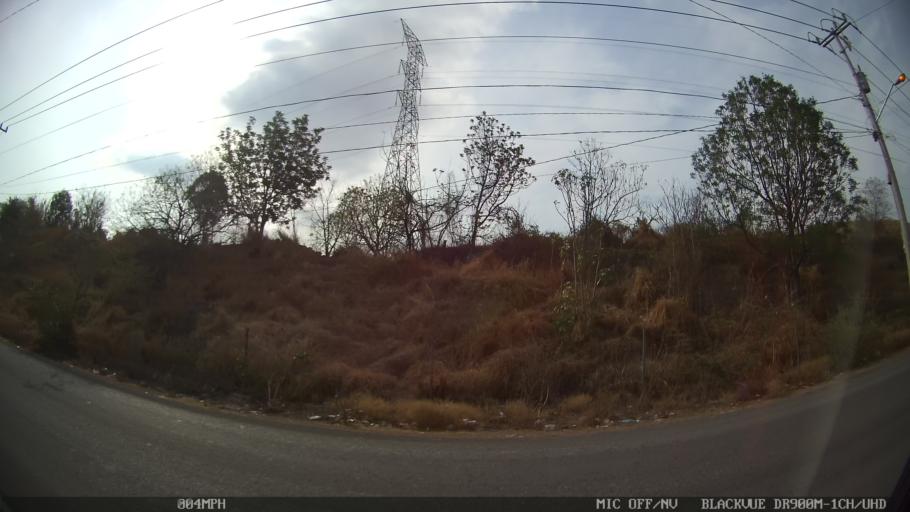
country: MX
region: Jalisco
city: Tonala
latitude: 20.6215
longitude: -103.2219
